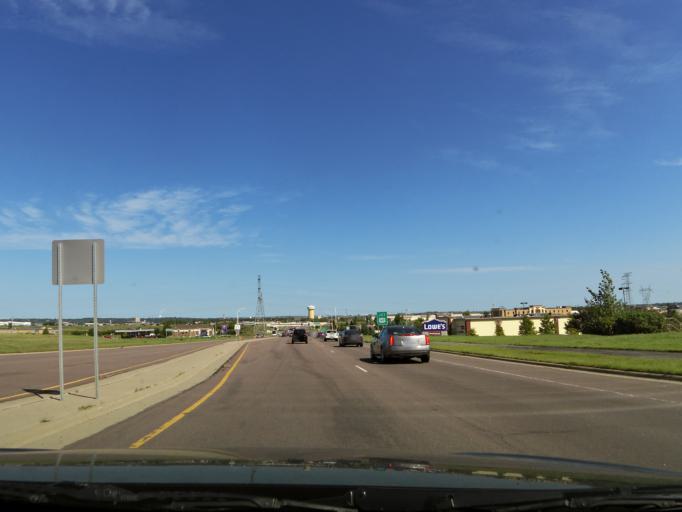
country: US
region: Minnesota
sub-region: Scott County
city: Shakopee
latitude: 44.7768
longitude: -93.4695
